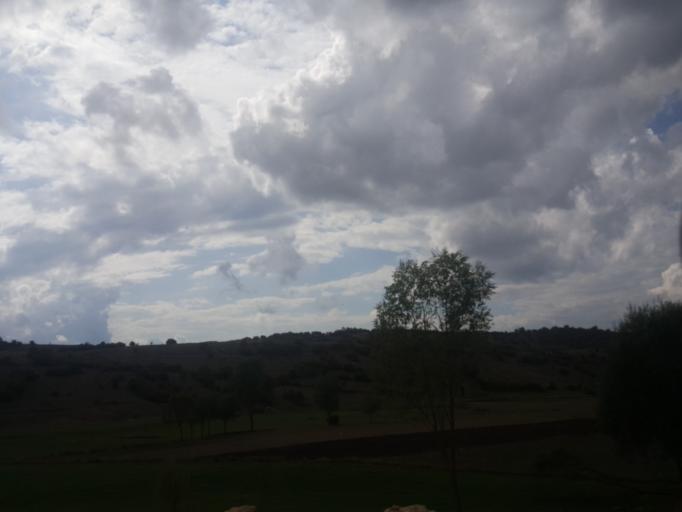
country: TR
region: Tokat
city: Bereketli
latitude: 40.5284
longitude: 37.2961
